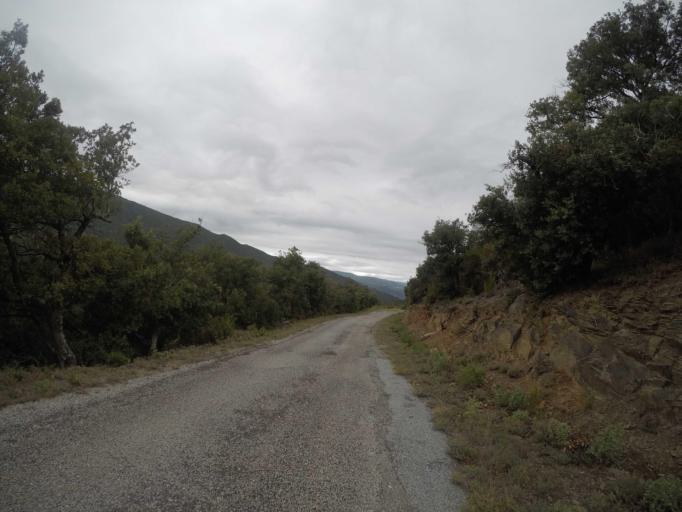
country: FR
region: Languedoc-Roussillon
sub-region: Departement des Pyrenees-Orientales
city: Ille-sur-Tet
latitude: 42.6144
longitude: 2.6099
